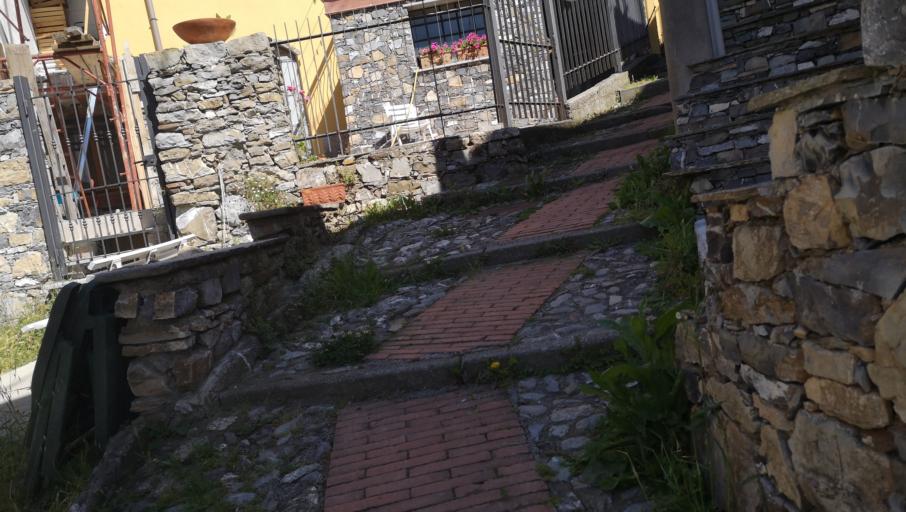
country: IT
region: Liguria
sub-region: Provincia di Genova
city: Piccarello
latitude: 44.4591
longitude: 8.9856
